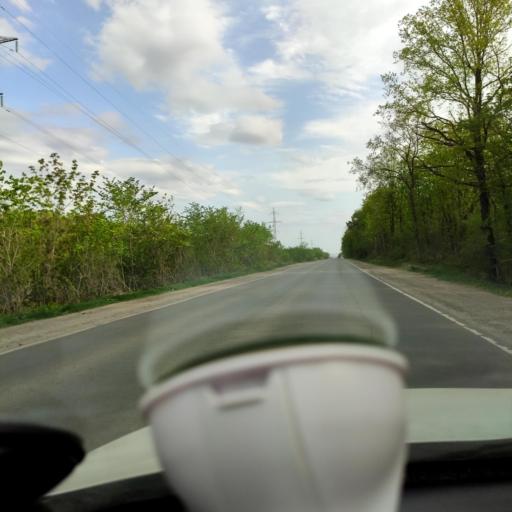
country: RU
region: Samara
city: Novosemeykino
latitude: 53.3386
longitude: 50.2499
